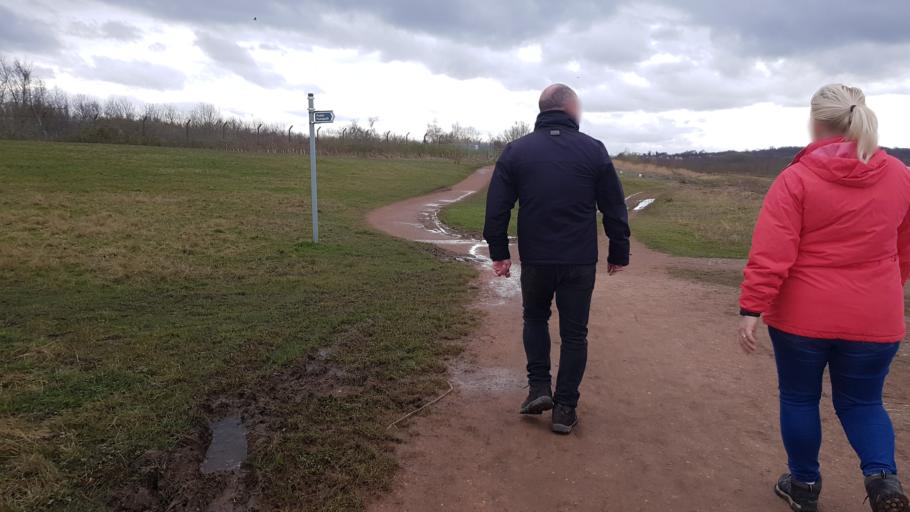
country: GB
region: England
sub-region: City and Borough of Leeds
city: Swillington
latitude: 53.7464
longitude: -1.3962
